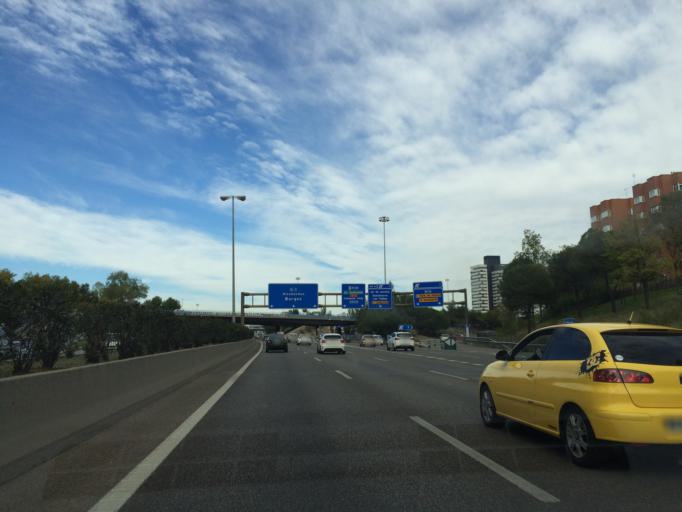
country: ES
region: Madrid
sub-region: Provincia de Madrid
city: Pinar de Chamartin
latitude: 40.4812
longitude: -3.6738
